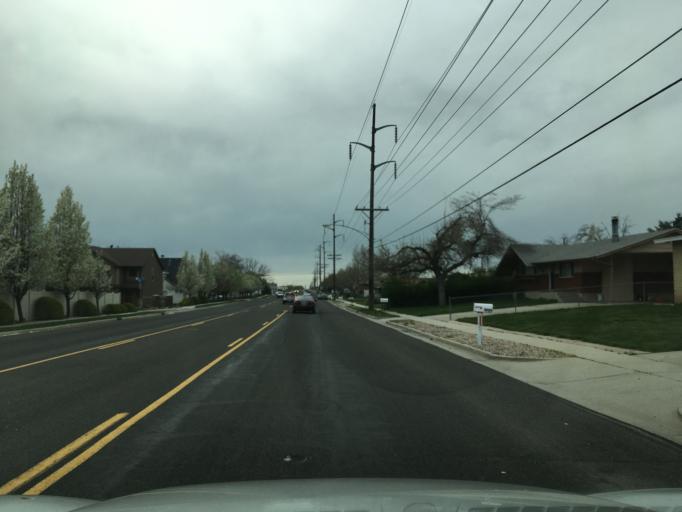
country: US
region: Utah
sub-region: Davis County
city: Layton
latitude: 41.0747
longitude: -111.9847
